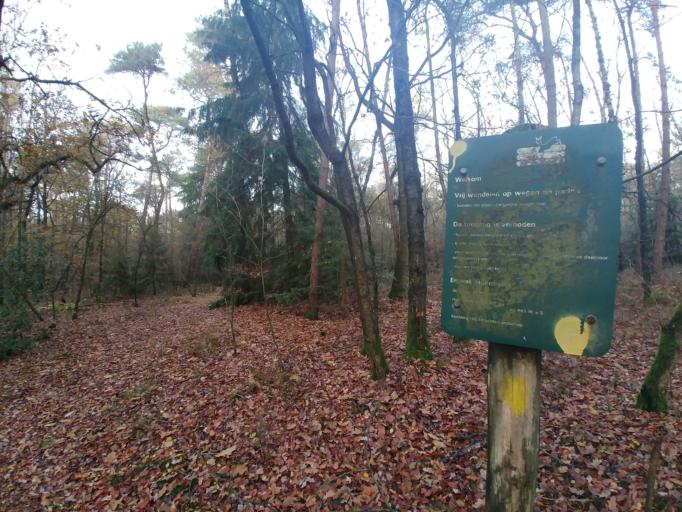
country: NL
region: Utrecht
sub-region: Gemeente Utrechtse Heuvelrug
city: Amerongen
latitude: 52.0220
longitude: 5.4733
